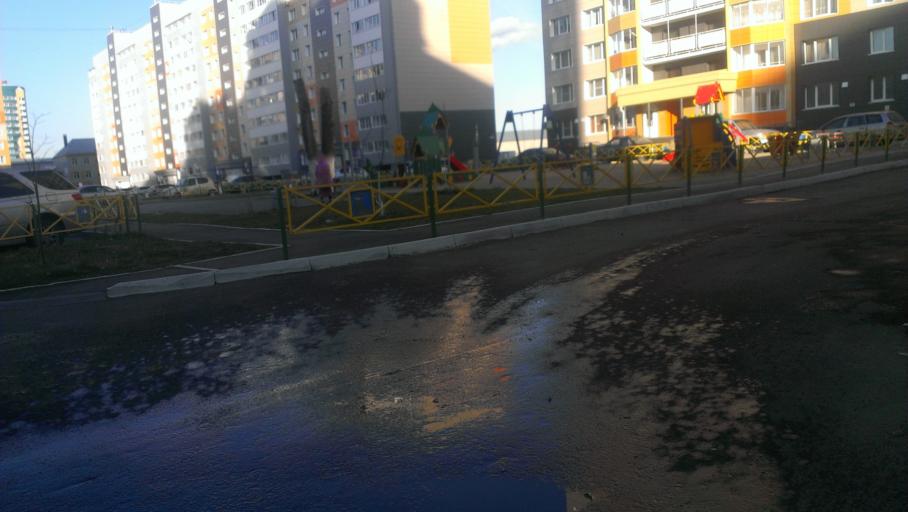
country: RU
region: Altai Krai
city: Novosilikatnyy
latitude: 53.3376
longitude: 83.6594
